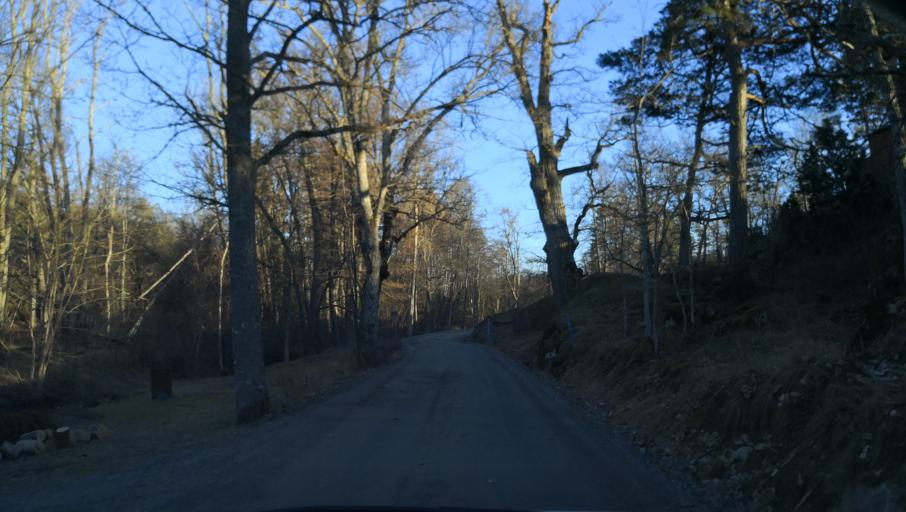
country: SE
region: Stockholm
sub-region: Varmdo Kommun
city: Mortnas
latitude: 59.3315
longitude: 18.4340
